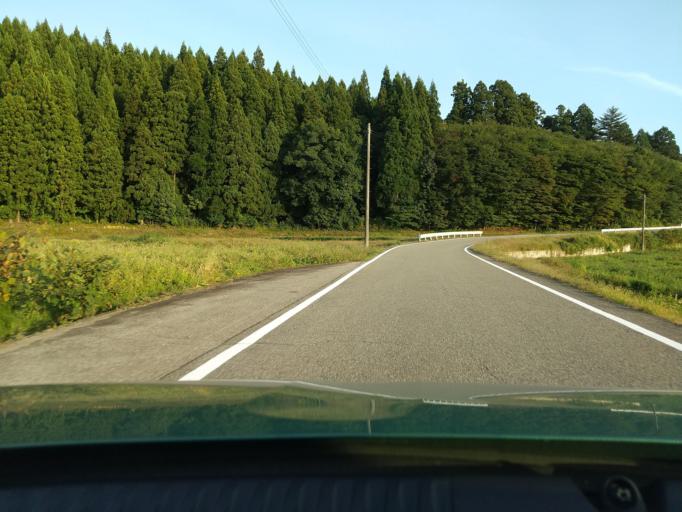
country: JP
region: Akita
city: Omagari
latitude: 39.4220
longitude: 140.5848
